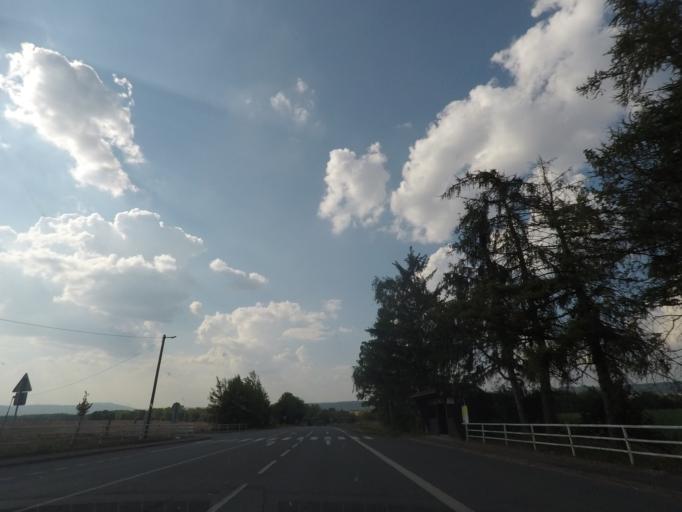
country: CZ
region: Kralovehradecky
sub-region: Okres Nachod
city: Jaromer
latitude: 50.4042
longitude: 15.8894
